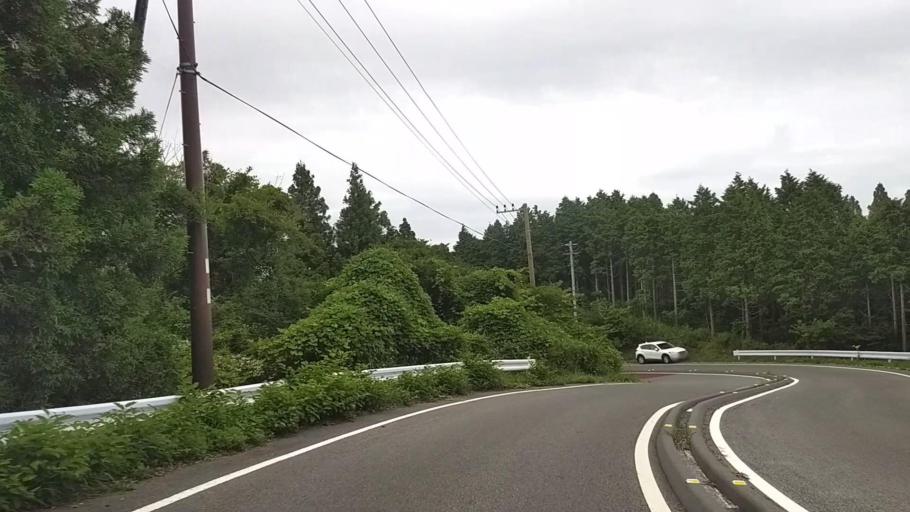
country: JP
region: Shizuoka
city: Gotemba
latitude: 35.3234
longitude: 139.0084
